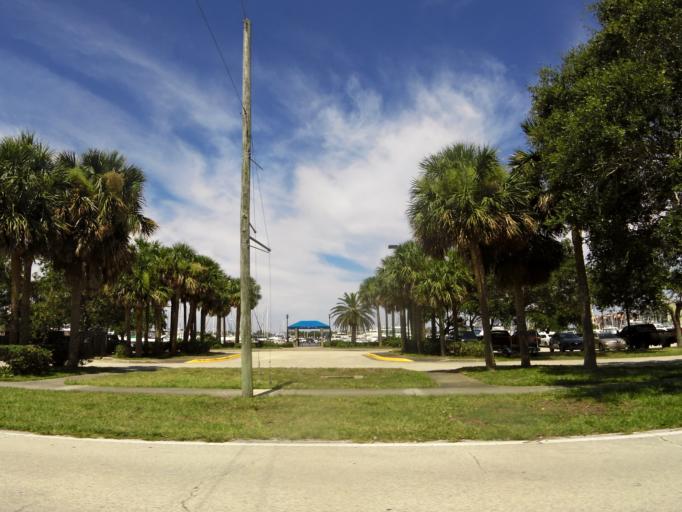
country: US
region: Florida
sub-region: Volusia County
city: Daytona Beach
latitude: 29.2040
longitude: -81.0157
